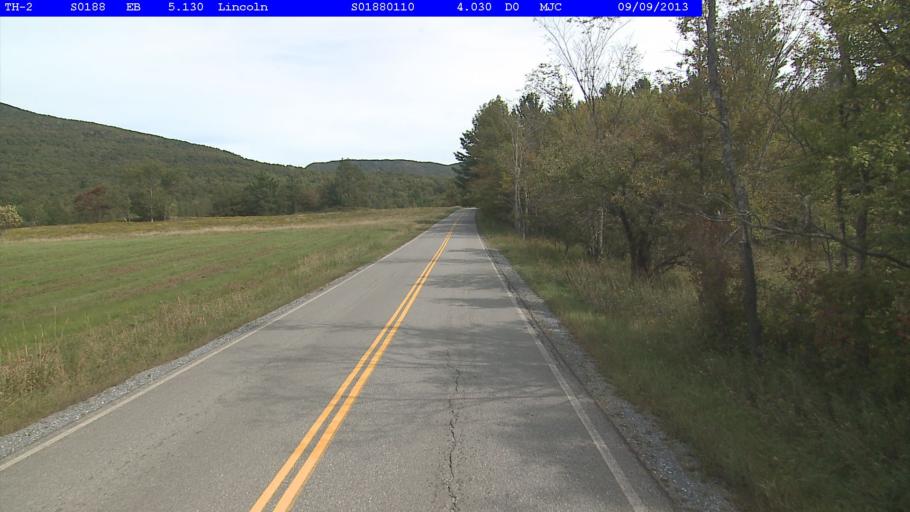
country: US
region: Vermont
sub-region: Addison County
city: Bristol
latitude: 44.0983
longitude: -72.9708
